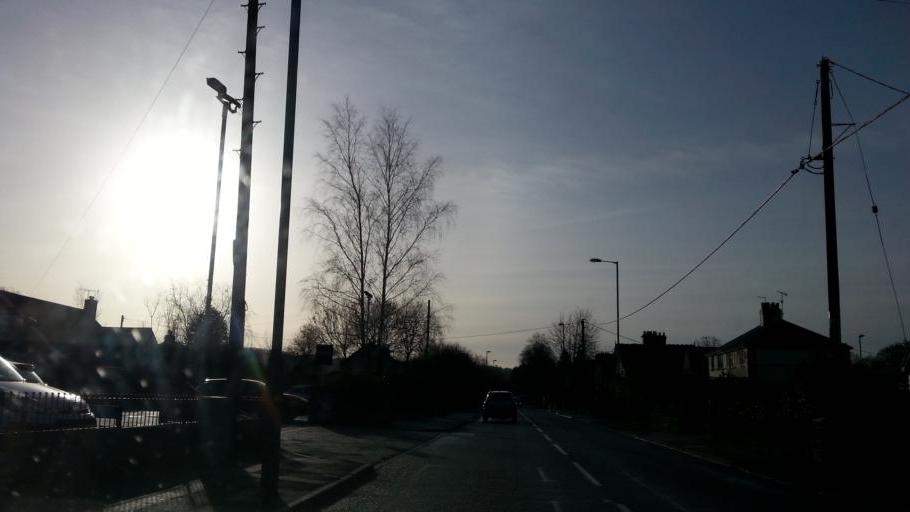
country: GB
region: England
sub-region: Staffordshire
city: Biddulph
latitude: 53.0708
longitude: -2.1172
